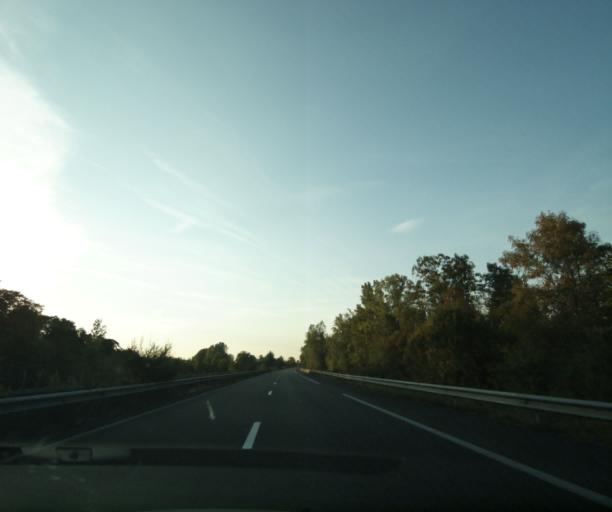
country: FR
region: Aquitaine
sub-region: Departement du Lot-et-Garonne
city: Layrac
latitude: 44.1324
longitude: 0.6794
